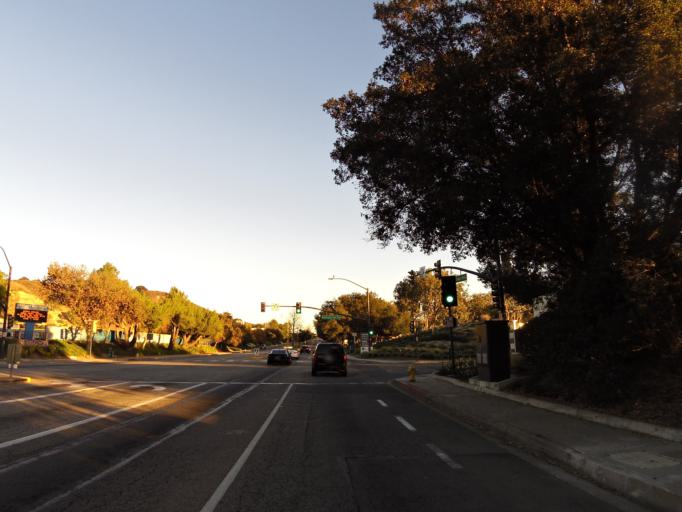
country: US
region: California
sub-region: Los Angeles County
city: Westlake Village
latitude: 34.1589
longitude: -118.8184
